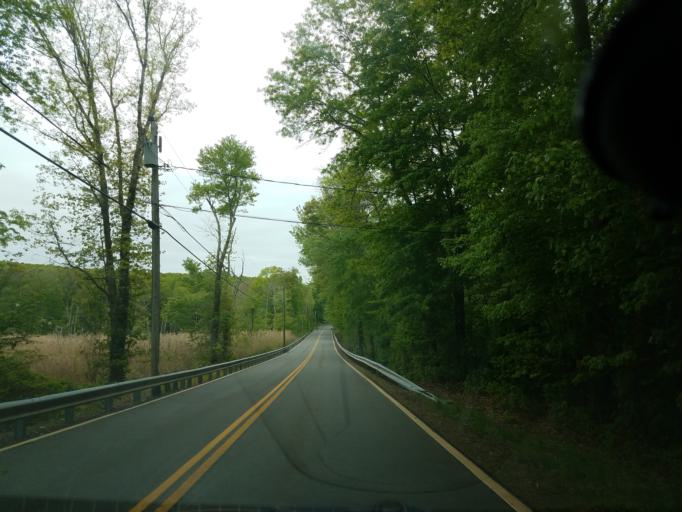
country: US
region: Connecticut
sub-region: Middlesex County
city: Higganum
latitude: 41.4010
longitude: -72.6046
